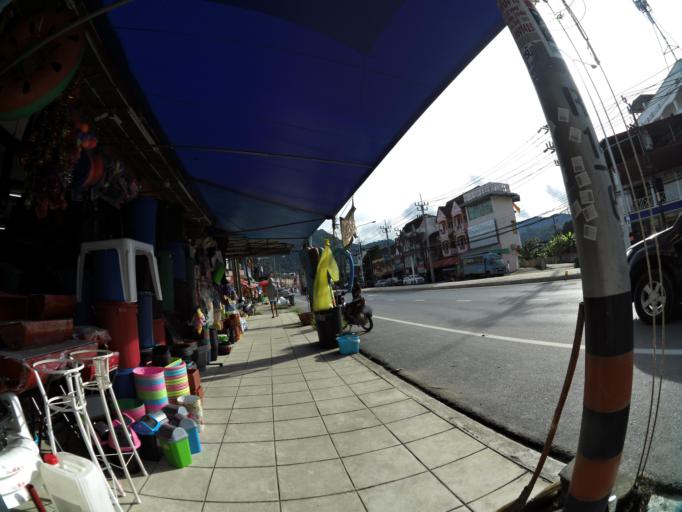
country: TH
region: Phuket
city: Patong
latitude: 7.9476
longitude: 98.2808
